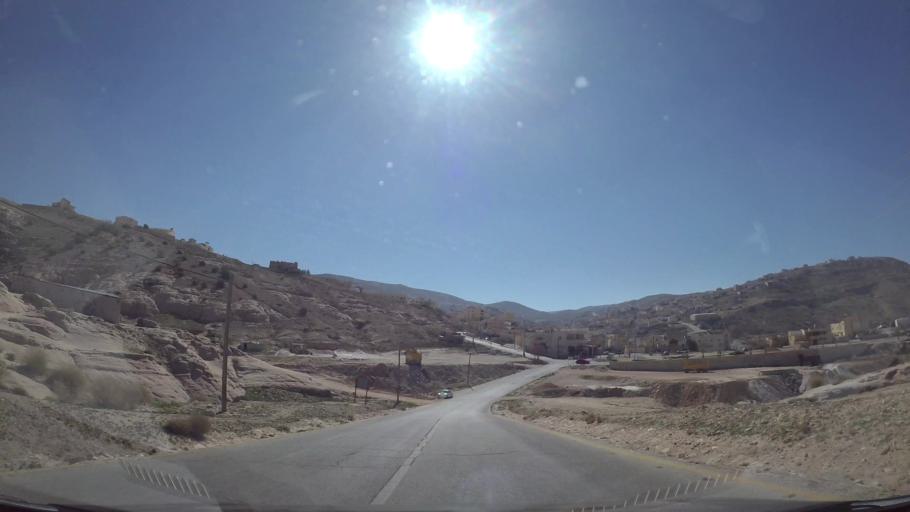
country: JO
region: Ma'an
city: Petra
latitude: 30.3296
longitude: 35.4695
